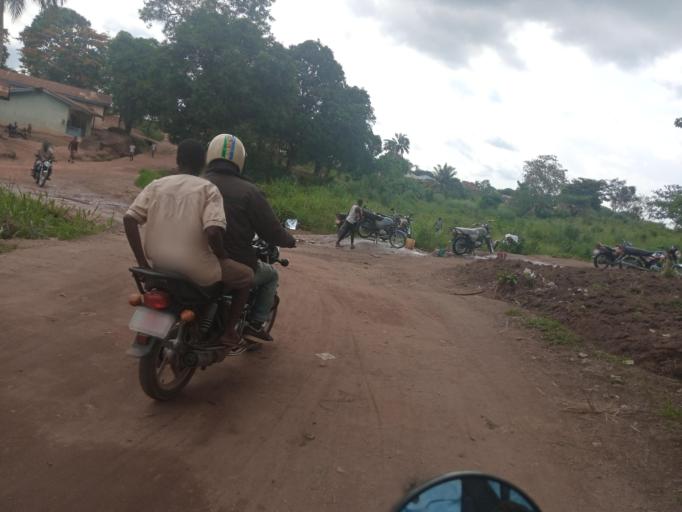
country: SL
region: Southern Province
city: Bo
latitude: 7.9818
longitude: -11.7393
